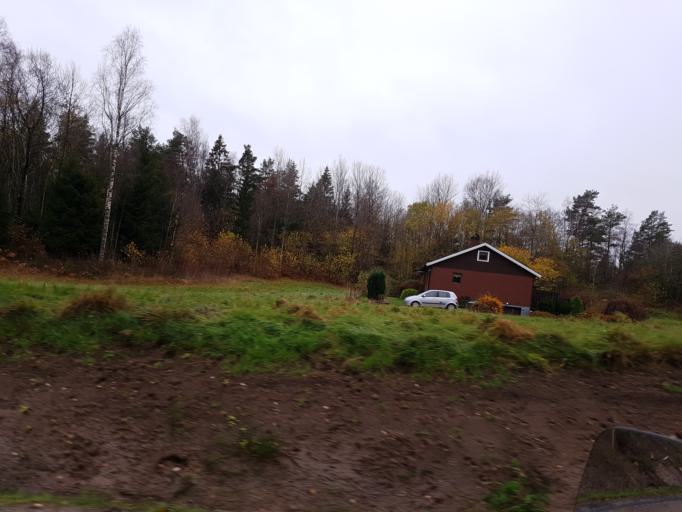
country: SE
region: Vaestra Goetaland
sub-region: Orust
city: Henan
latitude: 58.2418
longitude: 11.7282
